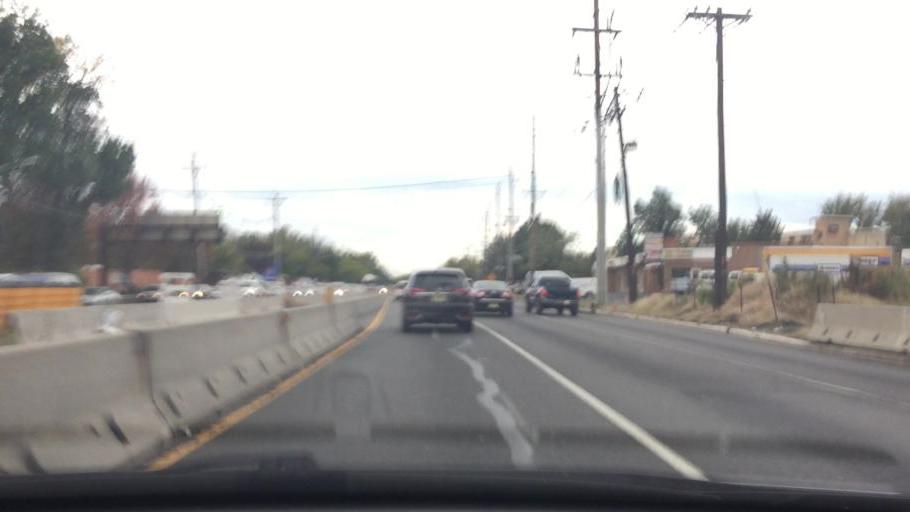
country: US
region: New Jersey
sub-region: Bergen County
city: Paramus
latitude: 40.9401
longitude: -74.0713
